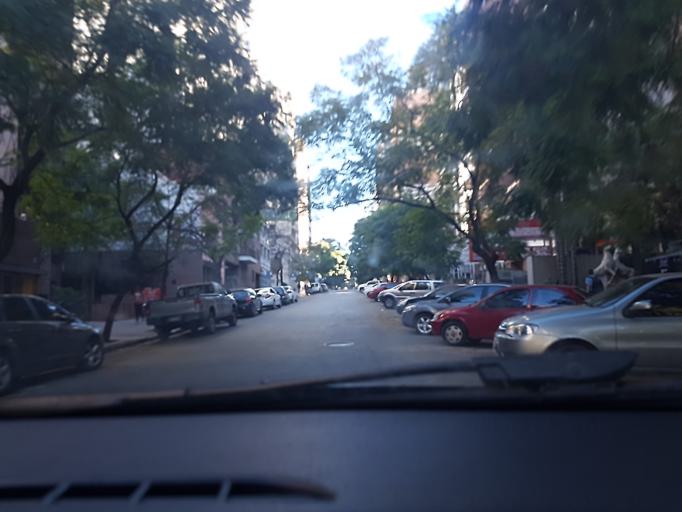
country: AR
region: Cordoba
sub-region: Departamento de Capital
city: Cordoba
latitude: -31.4240
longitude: -64.1800
